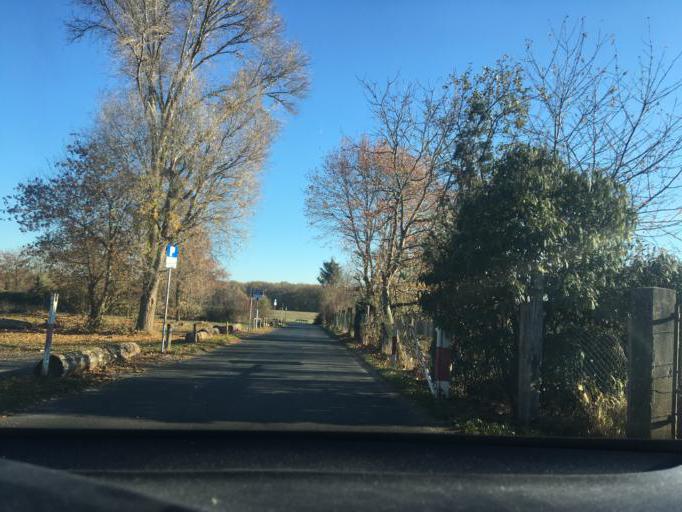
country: DE
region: Hesse
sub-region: Regierungsbezirk Darmstadt
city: Langenselbold
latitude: 50.1706
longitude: 9.0357
